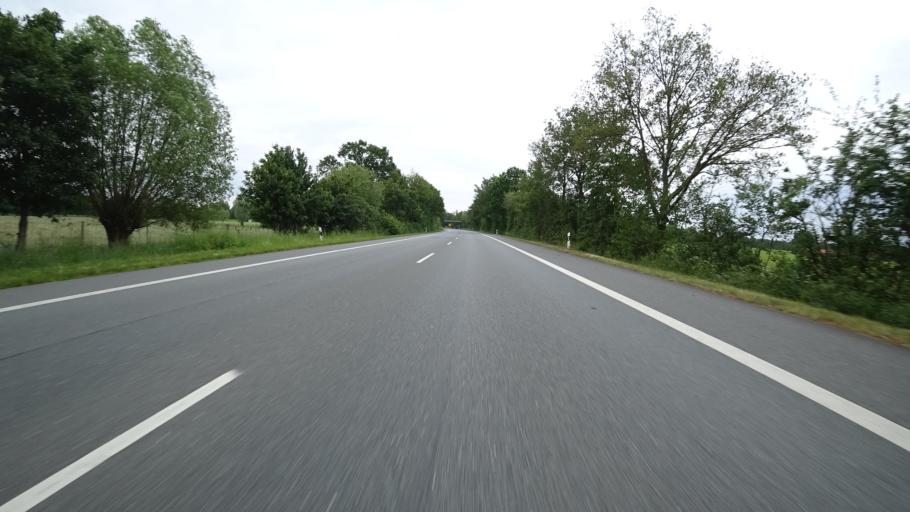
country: DE
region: North Rhine-Westphalia
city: Rietberg
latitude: 51.7982
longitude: 8.4136
